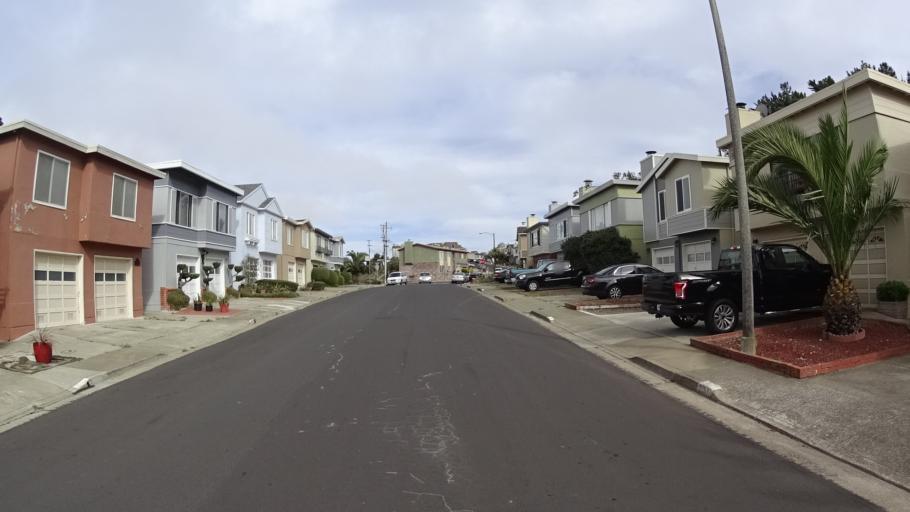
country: US
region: California
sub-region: San Mateo County
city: Daly City
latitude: 37.7042
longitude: -122.4395
